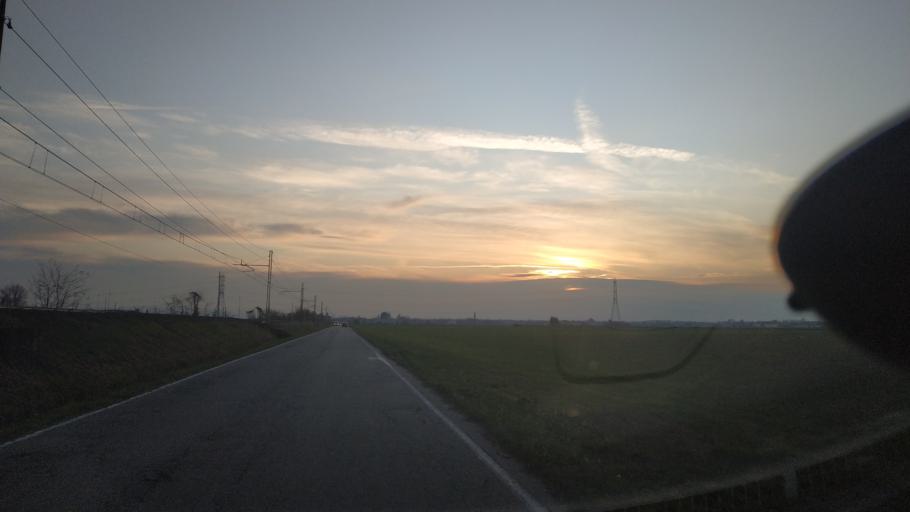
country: IT
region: Piedmont
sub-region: Provincia di Torino
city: Caluso
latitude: 45.2914
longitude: 7.8904
